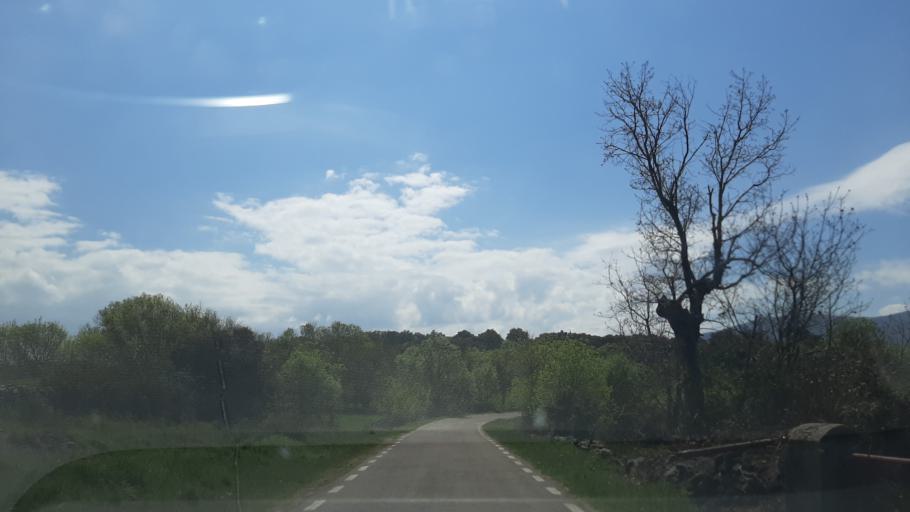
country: ES
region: Castille and Leon
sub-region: Provincia de Salamanca
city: Tejeda y Segoyuela
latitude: 40.6291
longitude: -6.0223
